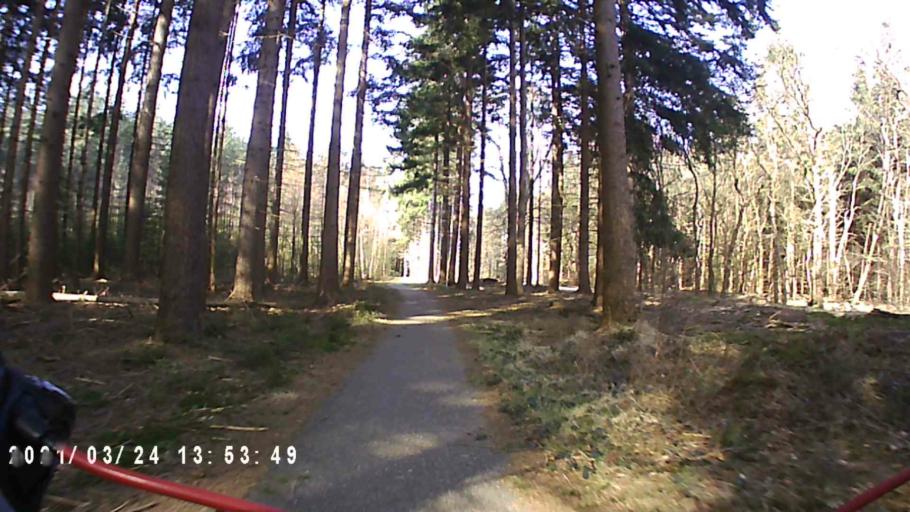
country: NL
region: Friesland
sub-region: Gemeente Smallingerland
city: Drachtstercompagnie
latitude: 53.0791
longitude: 6.2401
